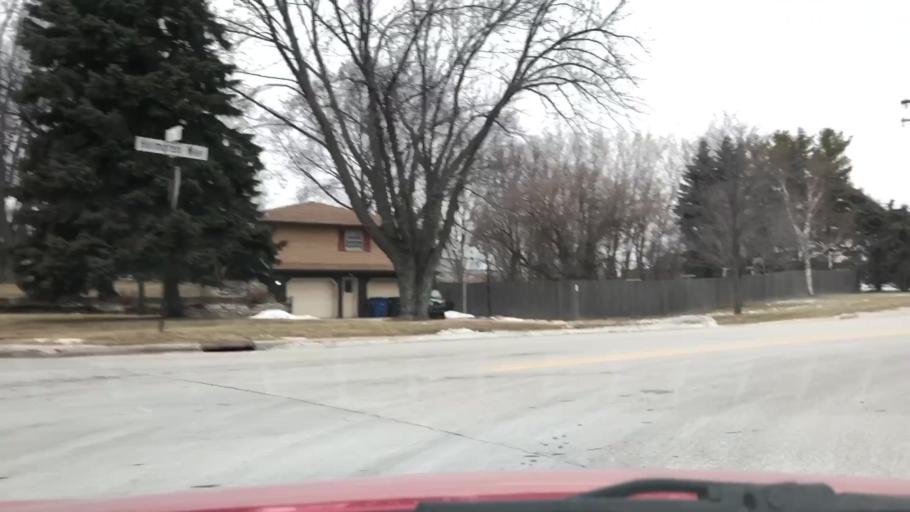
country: US
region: Wisconsin
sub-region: Brown County
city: De Pere
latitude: 44.4585
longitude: -88.0803
